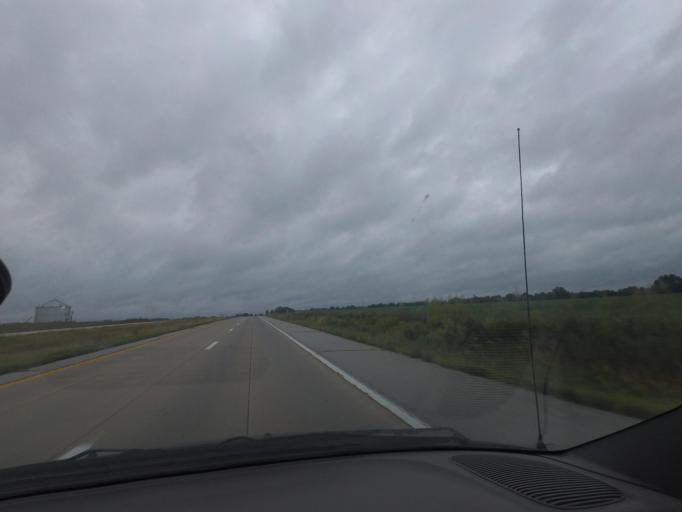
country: US
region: Missouri
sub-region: Marion County
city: Monroe City
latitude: 39.6735
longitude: -91.8720
